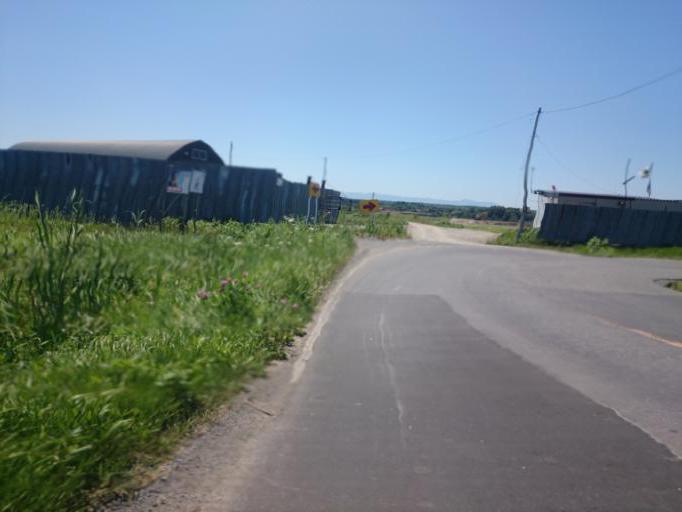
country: JP
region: Hokkaido
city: Ebetsu
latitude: 43.0705
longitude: 141.5580
